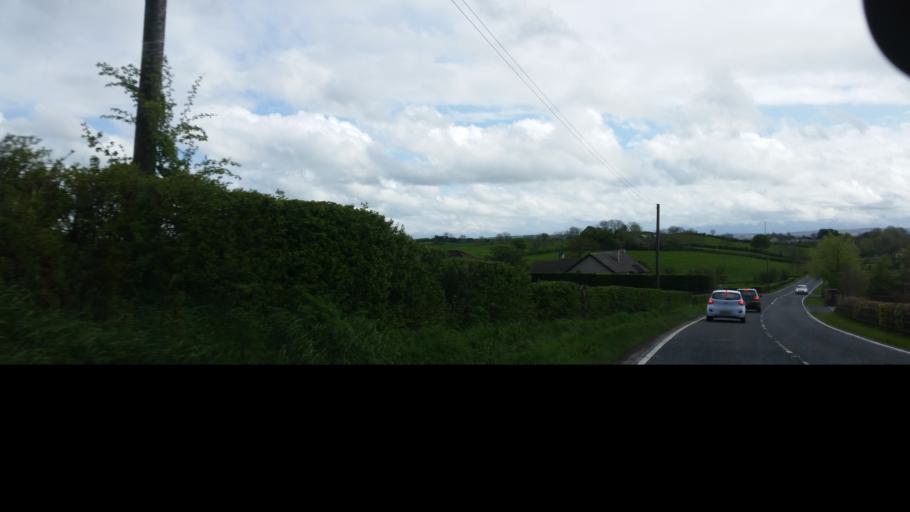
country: GB
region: Northern Ireland
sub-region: Omagh District
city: Omagh
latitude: 54.5540
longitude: -7.2829
